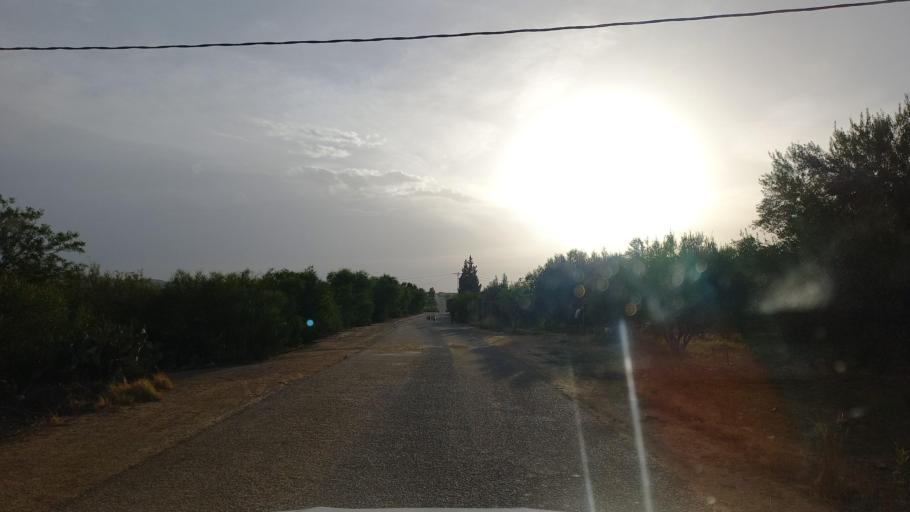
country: TN
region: Al Qasrayn
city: Kasserine
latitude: 35.2223
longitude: 9.0582
